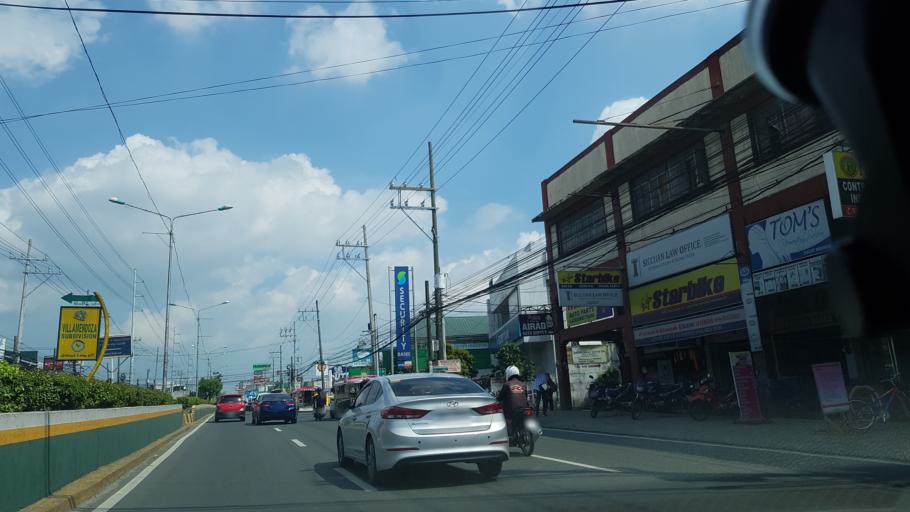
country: PH
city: Sambayanihan People's Village
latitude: 14.4681
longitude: 121.0129
